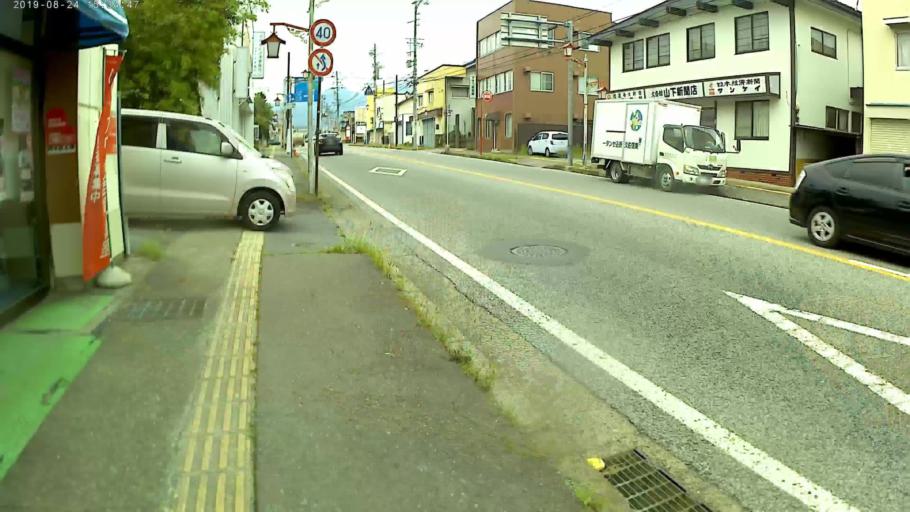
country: JP
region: Nagano
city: Saku
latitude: 36.2751
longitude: 138.4782
